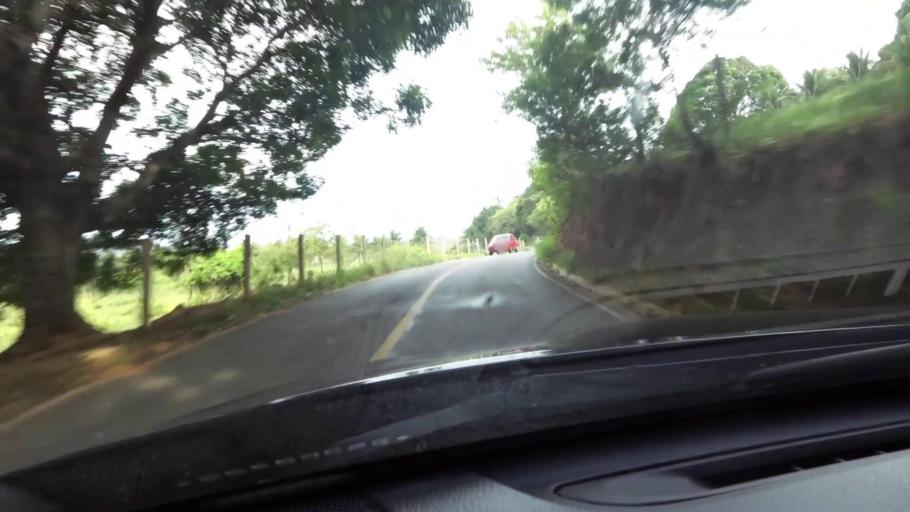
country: BR
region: Espirito Santo
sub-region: Guarapari
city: Guarapari
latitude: -20.6175
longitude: -40.5300
